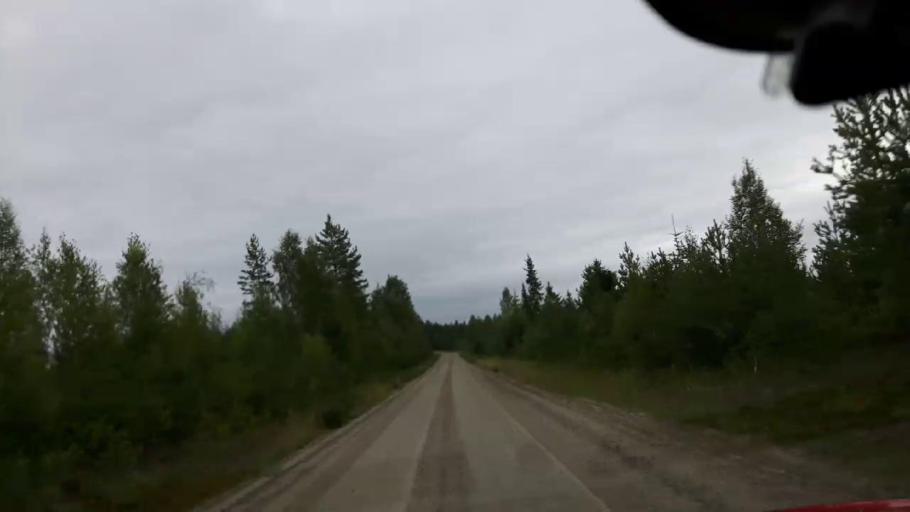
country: SE
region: Vaesternorrland
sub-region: Ange Kommun
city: Ange
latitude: 62.8059
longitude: 15.7459
